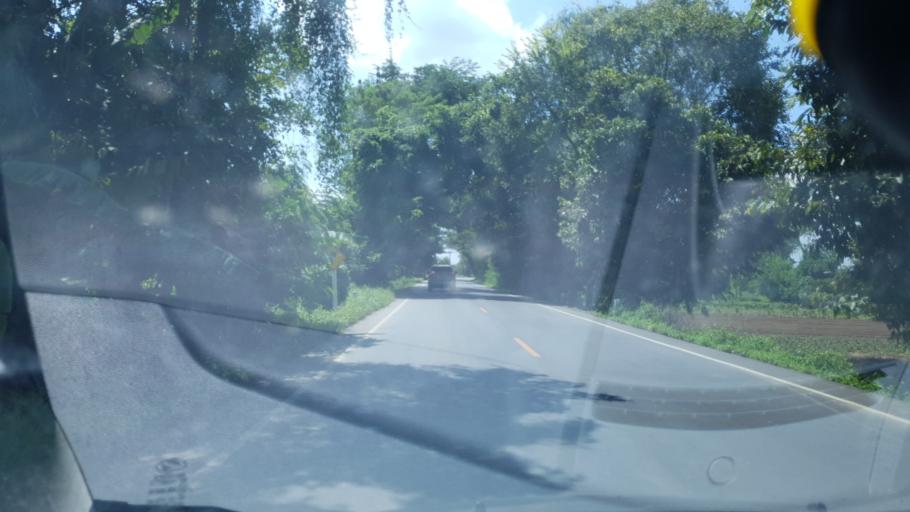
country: TH
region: Chiang Rai
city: Wiang Chai
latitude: 19.9653
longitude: 99.9625
